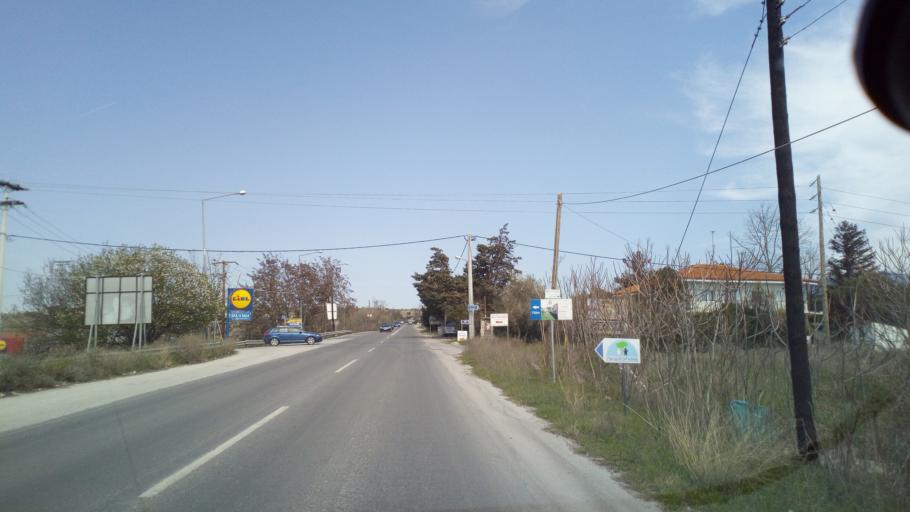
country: GR
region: Central Macedonia
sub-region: Nomos Thessalonikis
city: Thermi
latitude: 40.5598
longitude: 23.0220
